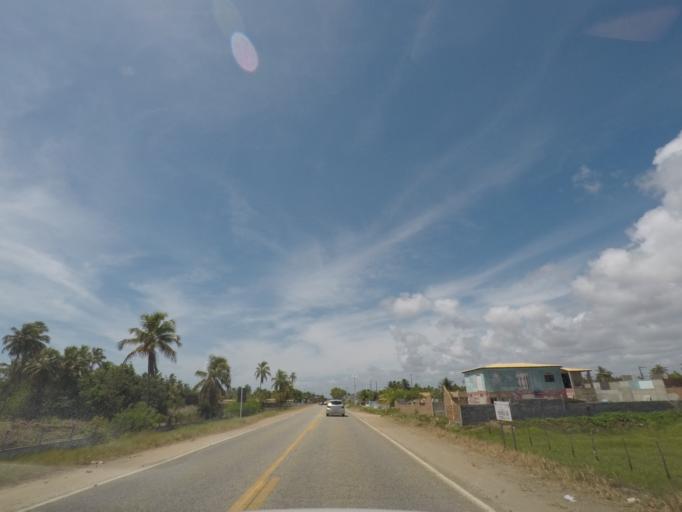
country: BR
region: Sergipe
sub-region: Sao Cristovao
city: Sao Cristovao
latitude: -11.2105
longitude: -37.2149
